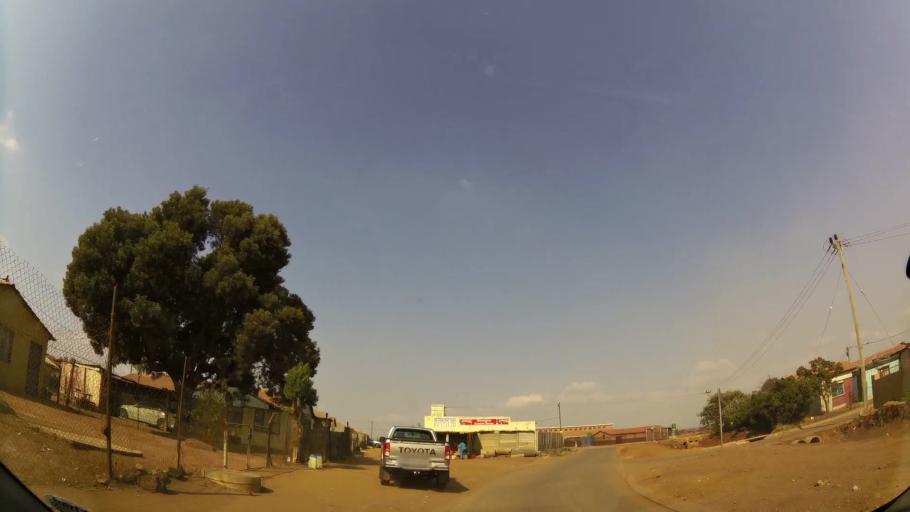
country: ZA
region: Gauteng
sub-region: Ekurhuleni Metropolitan Municipality
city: Springs
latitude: -26.1056
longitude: 28.4825
